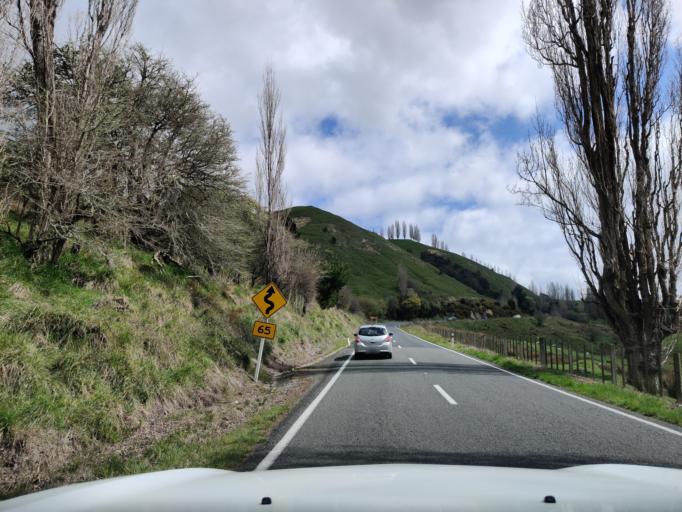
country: NZ
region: Manawatu-Wanganui
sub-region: Wanganui District
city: Wanganui
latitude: -39.7887
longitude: 175.2512
